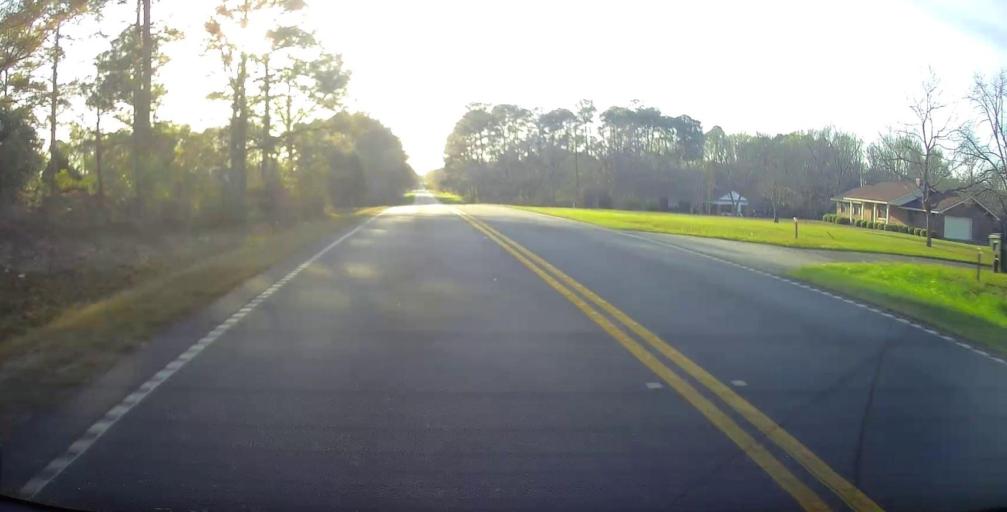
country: US
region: Georgia
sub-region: Evans County
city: Claxton
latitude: 32.1523
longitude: -81.8322
